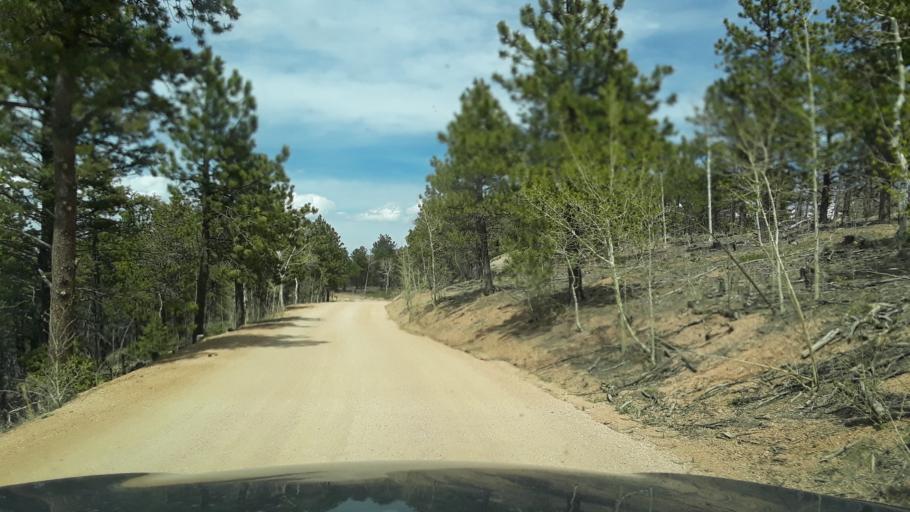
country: US
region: Colorado
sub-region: El Paso County
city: Palmer Lake
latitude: 39.0657
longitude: -104.9665
